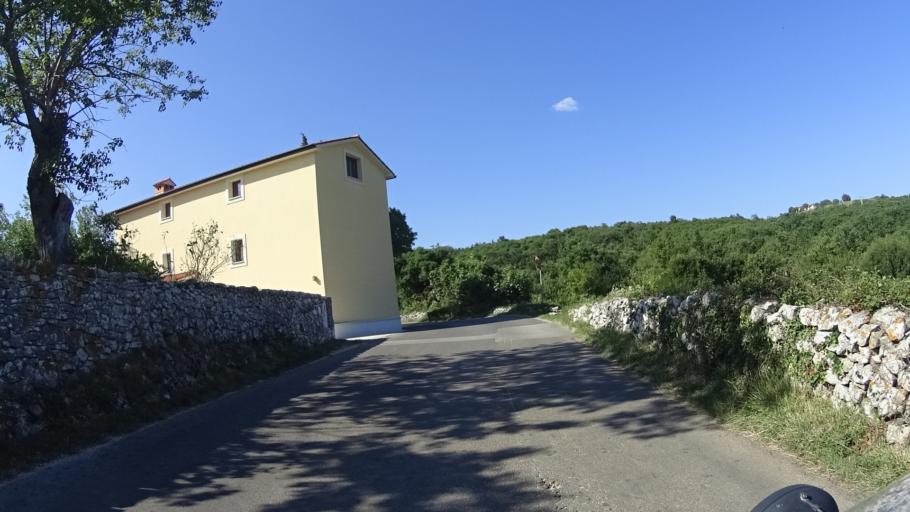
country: HR
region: Istarska
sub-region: Grad Labin
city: Labin
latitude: 45.0678
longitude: 14.1206
